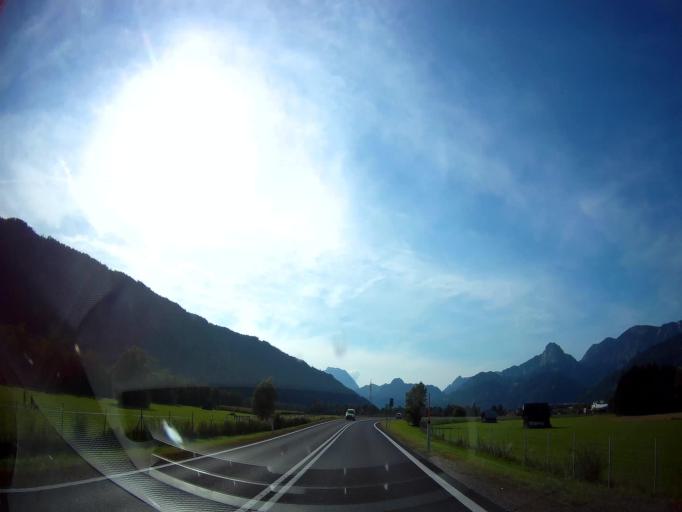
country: AT
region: Styria
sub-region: Politischer Bezirk Liezen
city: Liezen
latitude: 47.5553
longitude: 14.2677
